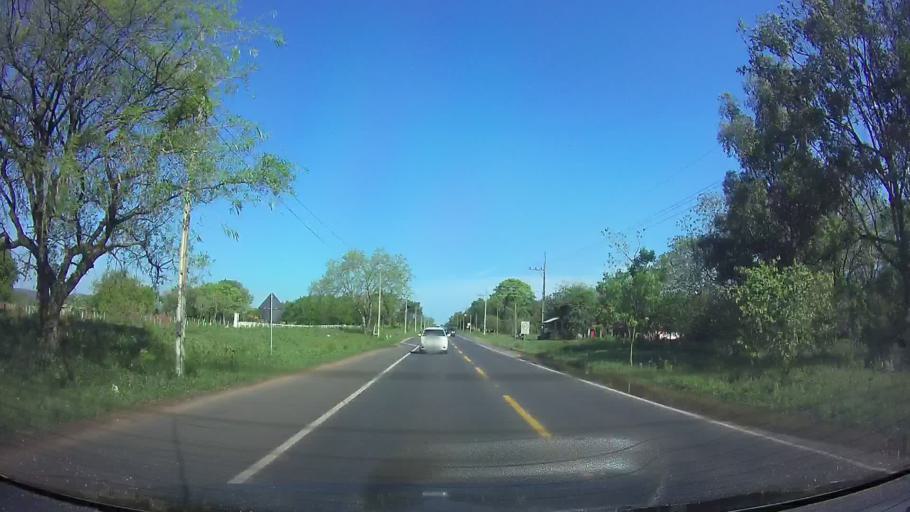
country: PY
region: Central
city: Ypacarai
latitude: -25.3832
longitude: -57.3000
